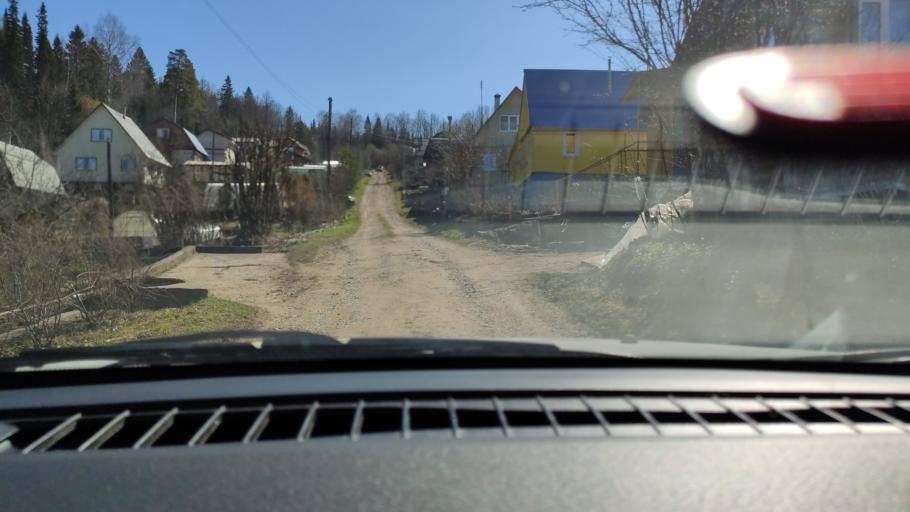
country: RU
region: Perm
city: Bershet'
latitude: 57.7225
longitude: 56.4099
